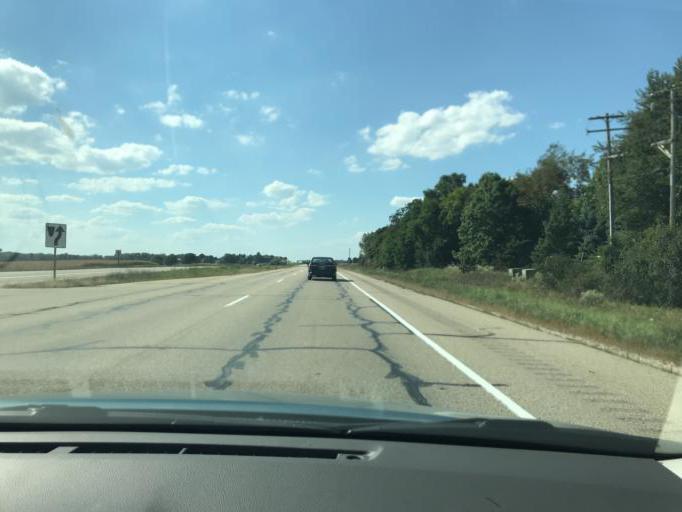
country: US
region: Wisconsin
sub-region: Kenosha County
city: Powers Lake
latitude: 42.5824
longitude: -88.2693
